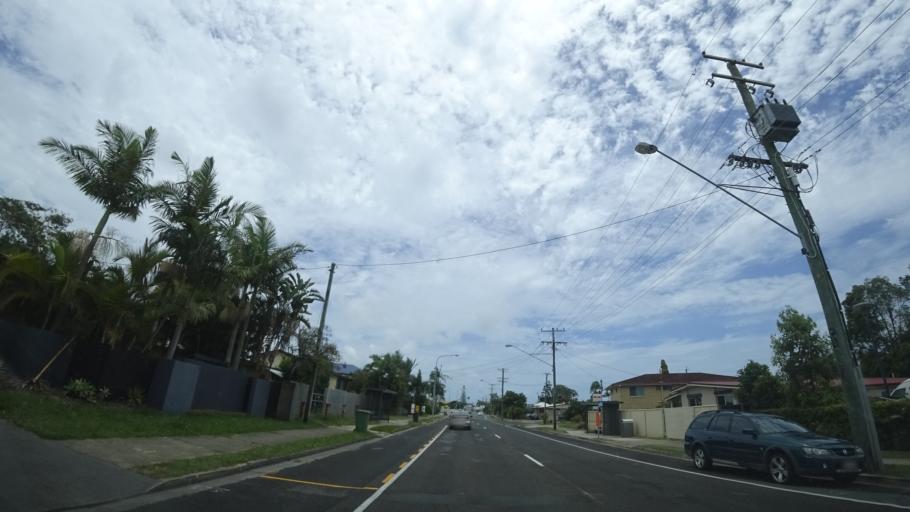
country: AU
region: Queensland
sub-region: Sunshine Coast
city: Mooloolaba
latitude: -26.6626
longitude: 153.0926
